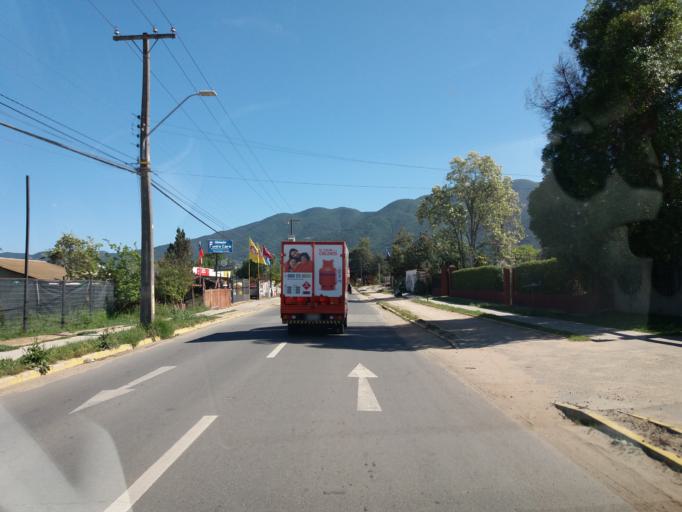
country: CL
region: Valparaiso
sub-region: Provincia de Marga Marga
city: Limache
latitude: -33.0043
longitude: -71.1740
